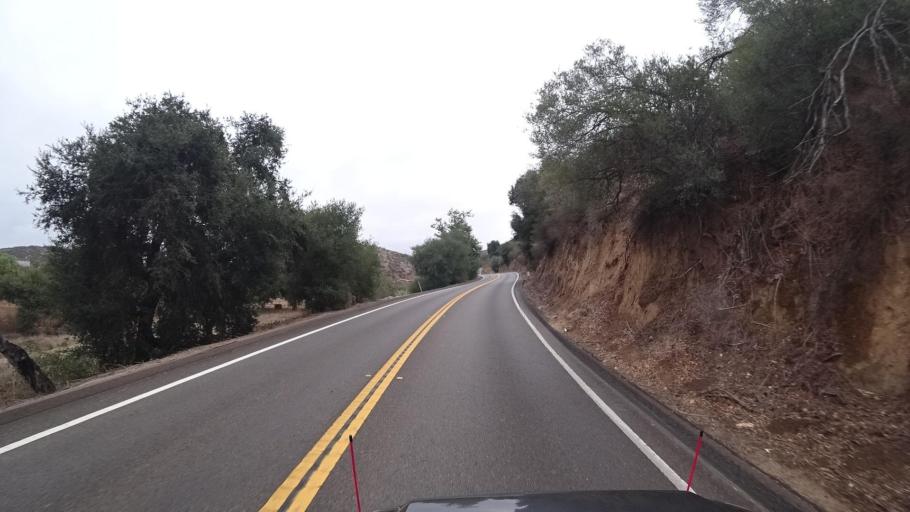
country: US
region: California
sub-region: San Diego County
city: Ramona
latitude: 33.0717
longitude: -116.8991
